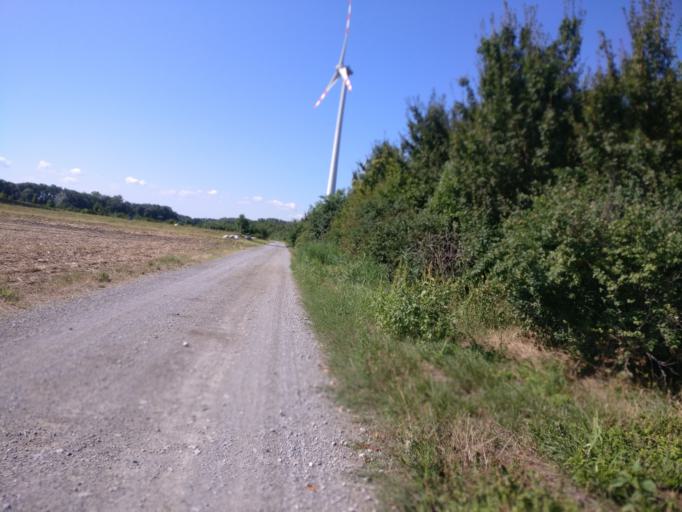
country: AT
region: Lower Austria
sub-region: Politischer Bezirk Baden
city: Ebreichsdorf
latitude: 47.9352
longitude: 16.3736
